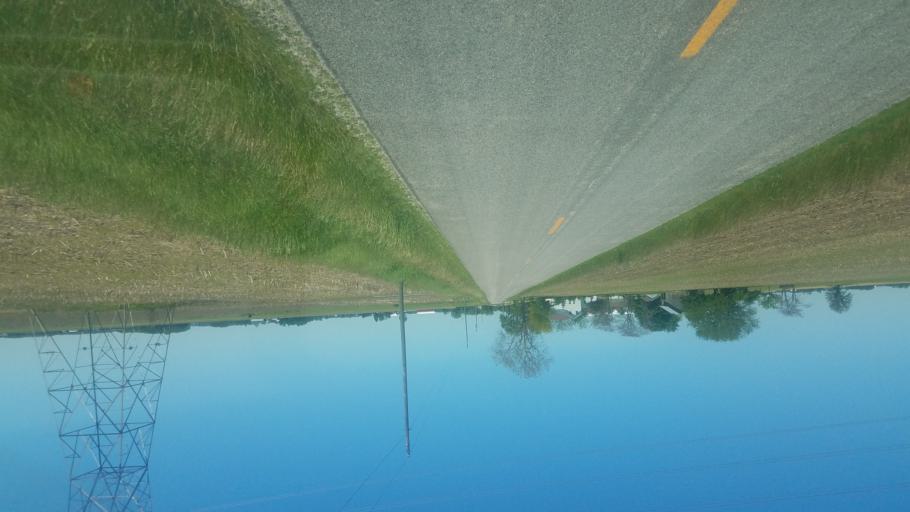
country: US
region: Ohio
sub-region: Shelby County
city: Sidney
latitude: 40.2094
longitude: -84.0934
